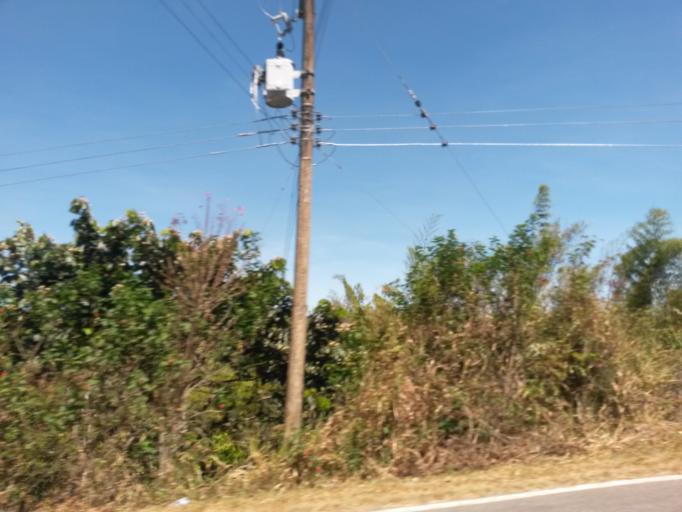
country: CO
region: Cauca
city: Lopez
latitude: 2.4423
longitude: -76.7914
